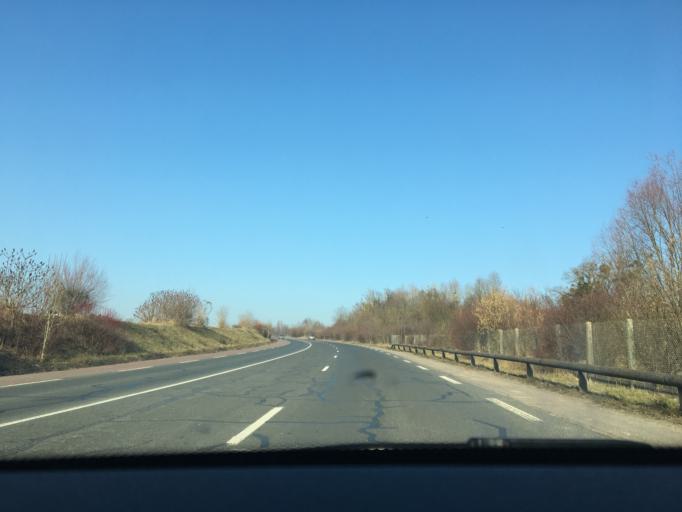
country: FR
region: Ile-de-France
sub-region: Departement des Yvelines
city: Limay
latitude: 48.9985
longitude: 1.7503
